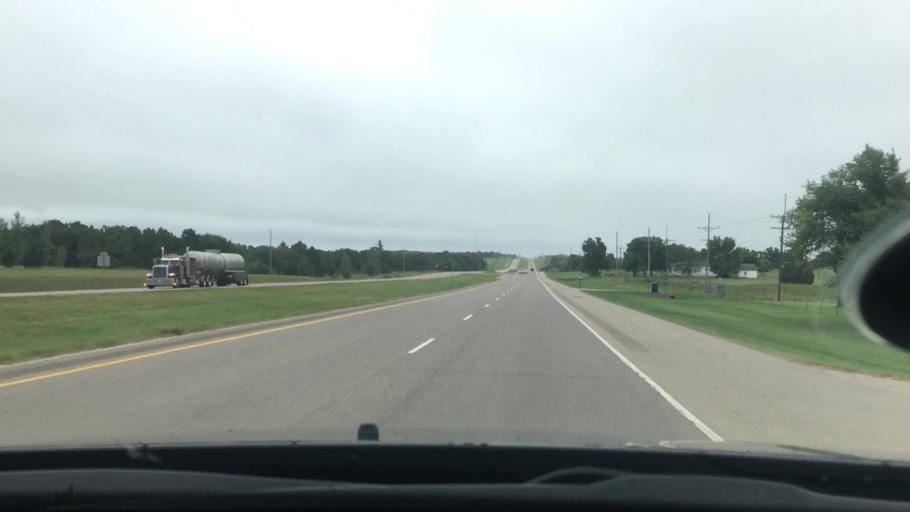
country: US
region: Oklahoma
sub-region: Seminole County
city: Seminole
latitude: 35.3517
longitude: -96.6715
